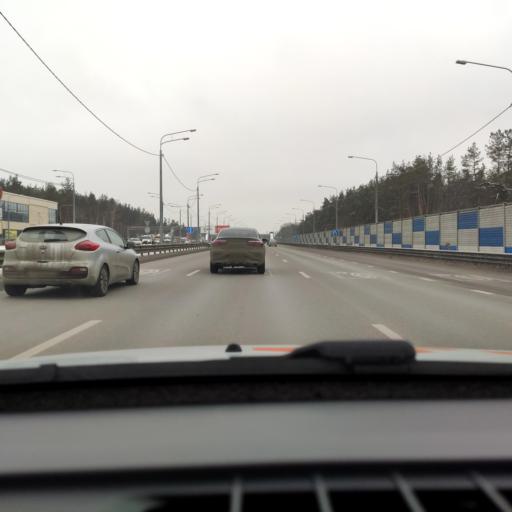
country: RU
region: Voronezj
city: Podgornoye
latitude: 51.7439
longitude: 39.1866
